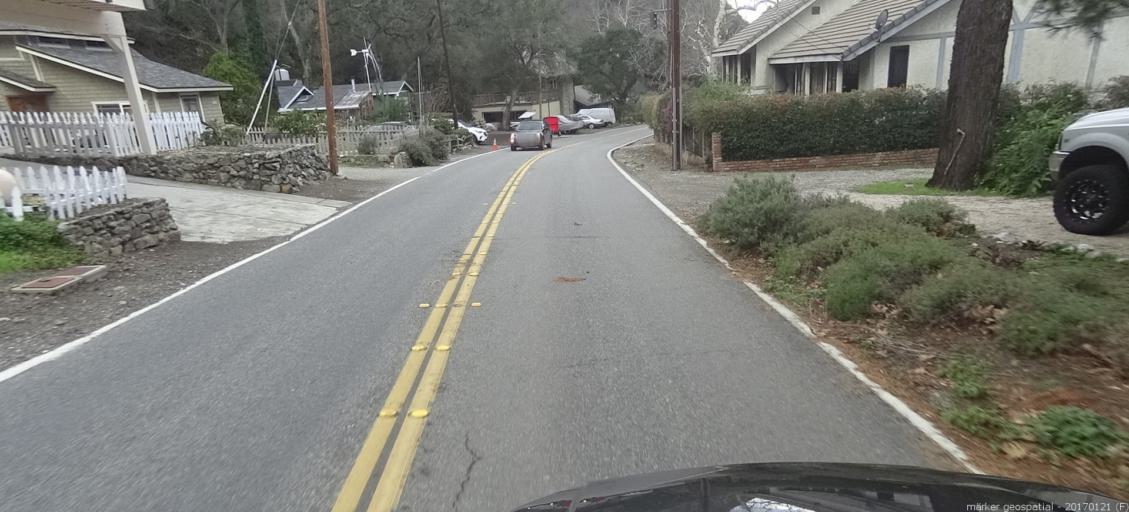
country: US
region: California
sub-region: Orange County
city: Portola Hills
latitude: 33.7461
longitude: -117.6273
